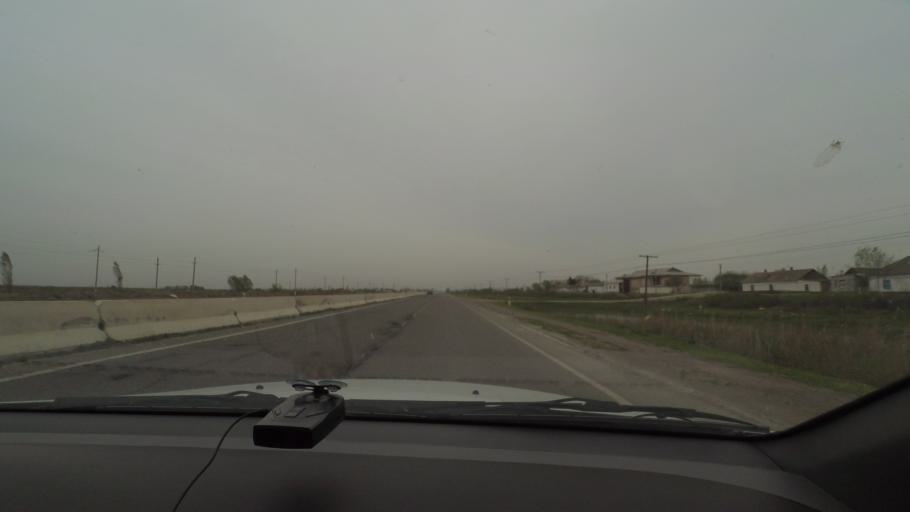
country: UZ
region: Sirdaryo
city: Guliston
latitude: 40.4954
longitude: 68.6364
